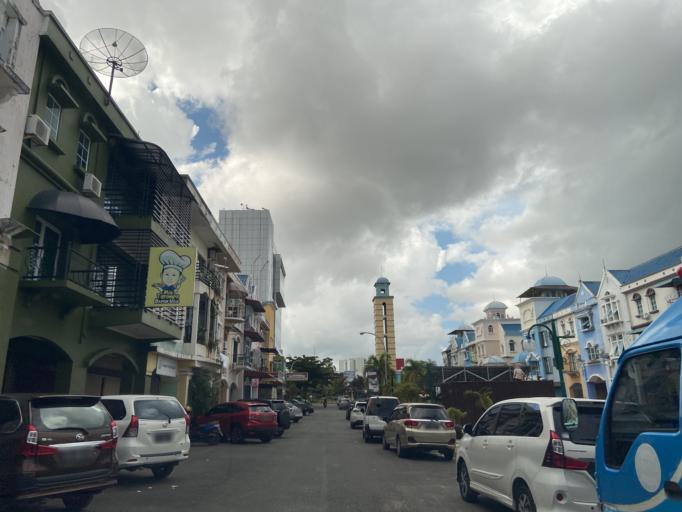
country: SG
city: Singapore
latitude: 1.1081
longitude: 104.0276
